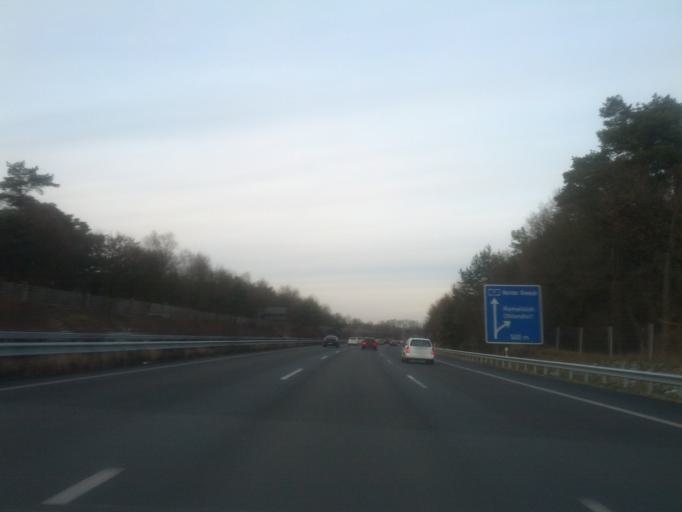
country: DE
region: Lower Saxony
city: Marxen
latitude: 53.3332
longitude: 10.0420
